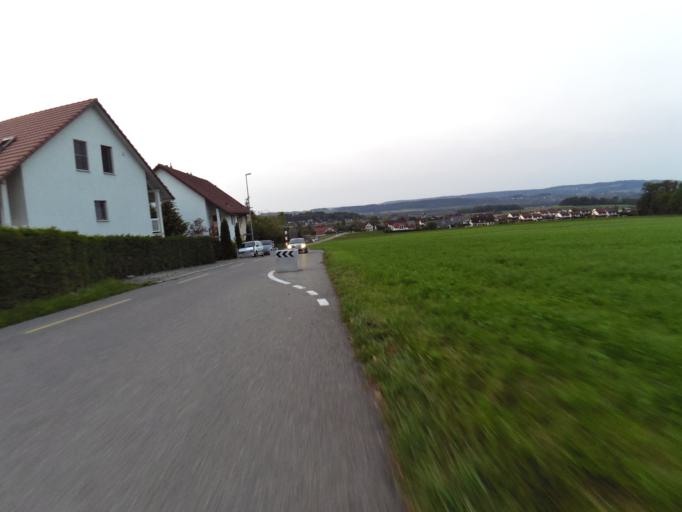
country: CH
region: Thurgau
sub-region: Frauenfeld District
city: Gachnang
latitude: 47.5475
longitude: 8.8632
